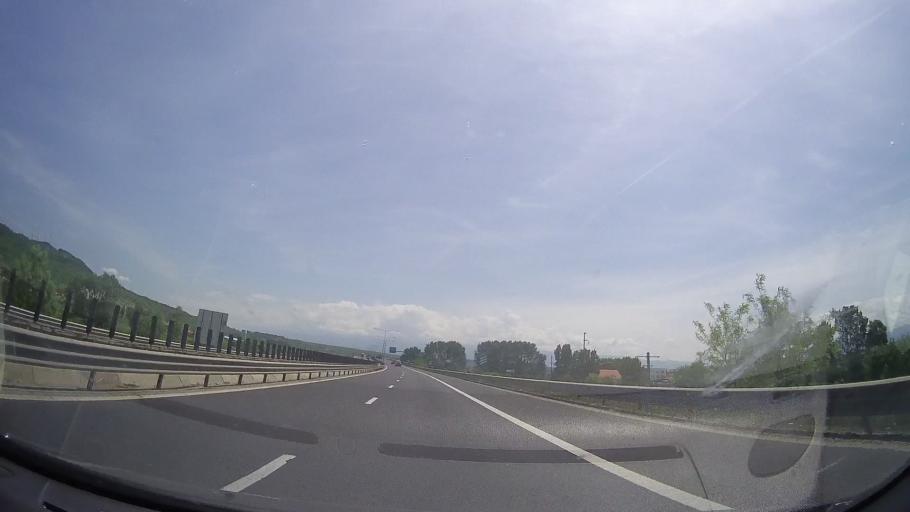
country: RO
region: Sibiu
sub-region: Municipiul Sibiu
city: Sibiu
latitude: 45.8049
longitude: 24.1794
